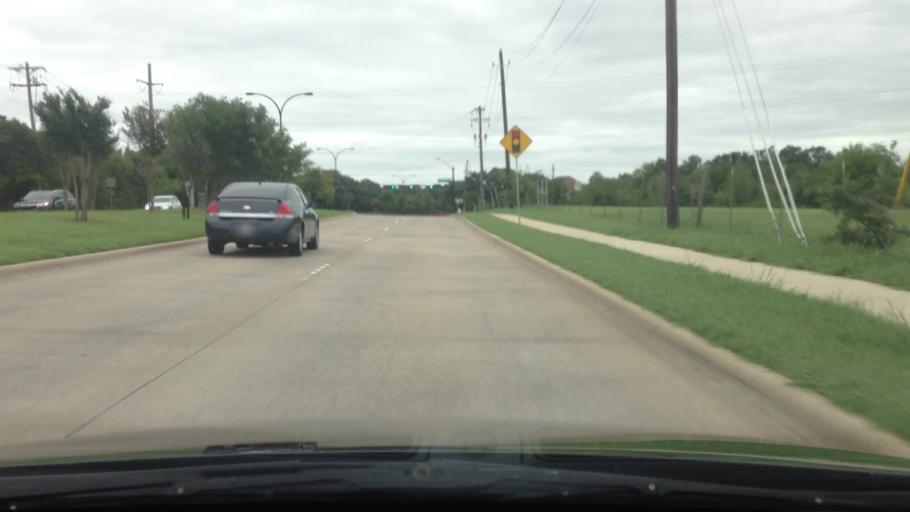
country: US
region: Texas
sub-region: Tarrant County
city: Keller
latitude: 32.9114
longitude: -97.2324
